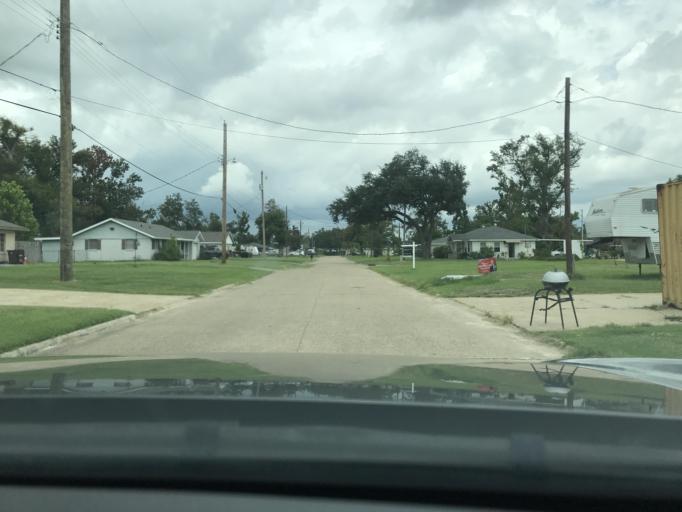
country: US
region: Louisiana
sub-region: Calcasieu Parish
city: Westlake
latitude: 30.2485
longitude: -93.2549
